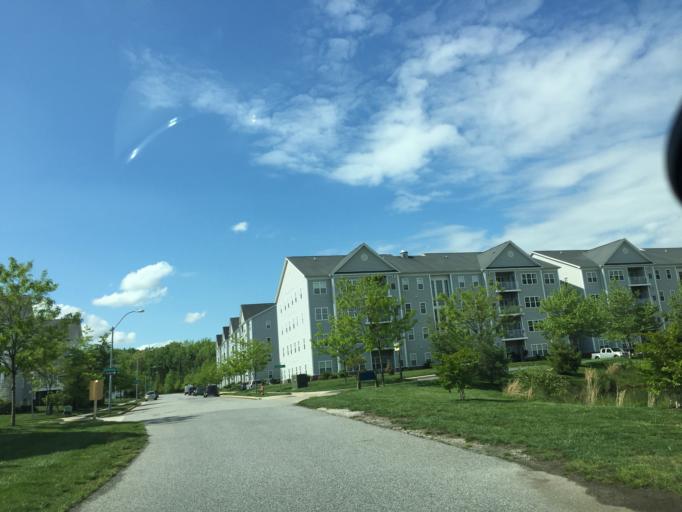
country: US
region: Maryland
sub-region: Baltimore County
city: Middle River
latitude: 39.3136
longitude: -76.4376
